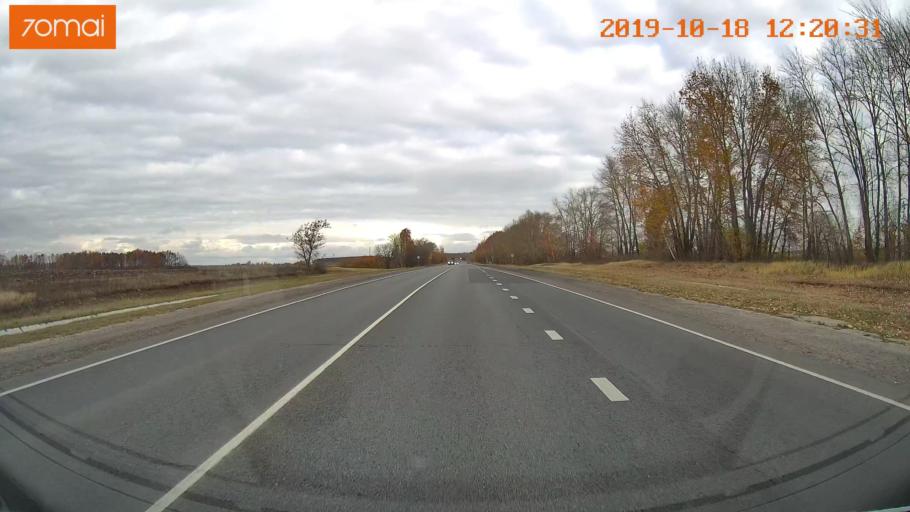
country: RU
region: Rjazan
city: Bagramovo
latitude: 54.4988
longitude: 39.4812
